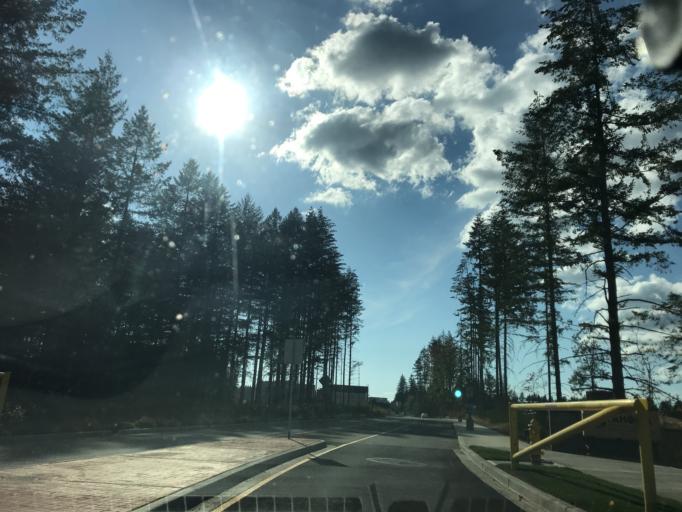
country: US
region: Washington
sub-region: King County
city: Ravensdale
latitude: 47.3580
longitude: -122.0229
